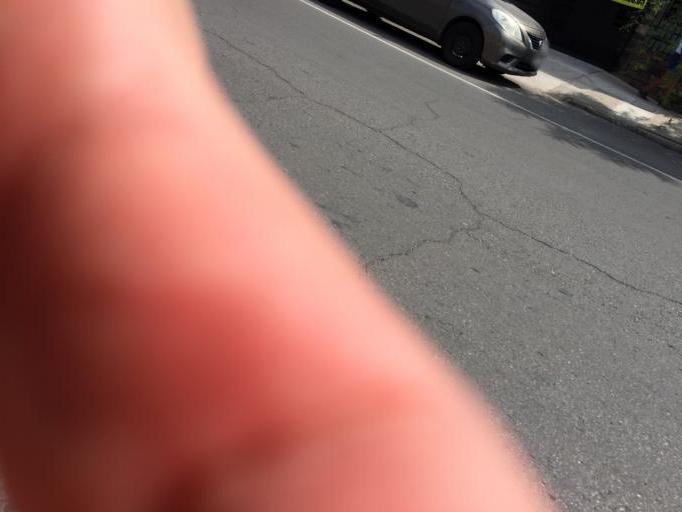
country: MX
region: Sonora
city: Hermosillo
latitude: 29.1095
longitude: -110.9661
